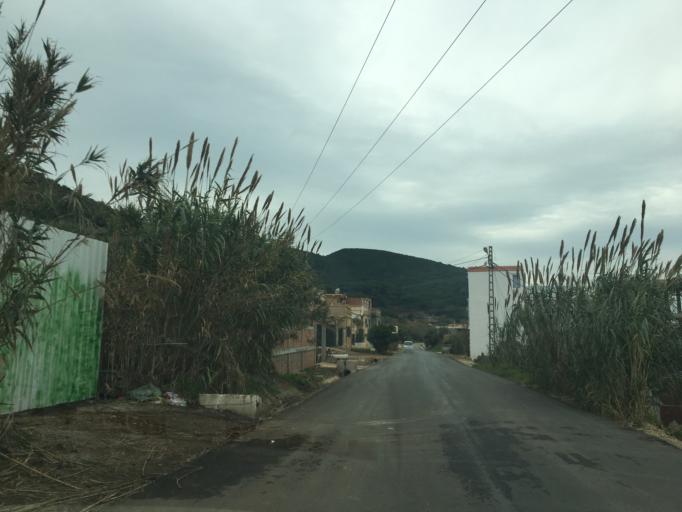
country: DZ
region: Tipaza
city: Tipasa
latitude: 36.6348
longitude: 2.3029
